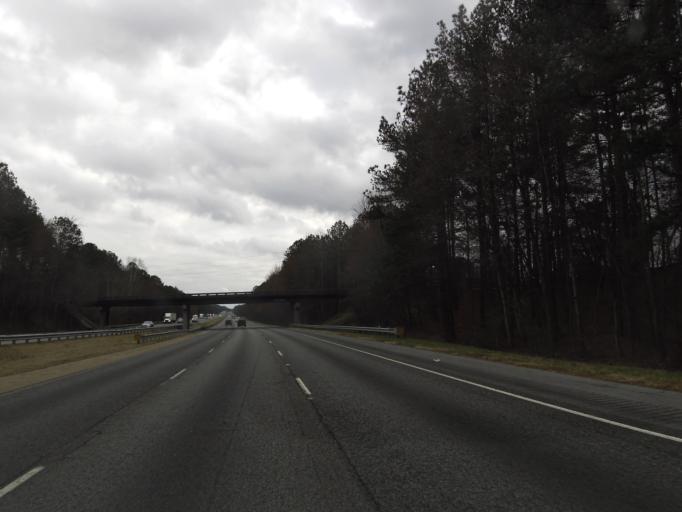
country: US
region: Georgia
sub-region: Gordon County
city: Calhoun
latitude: 34.6334
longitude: -84.9762
